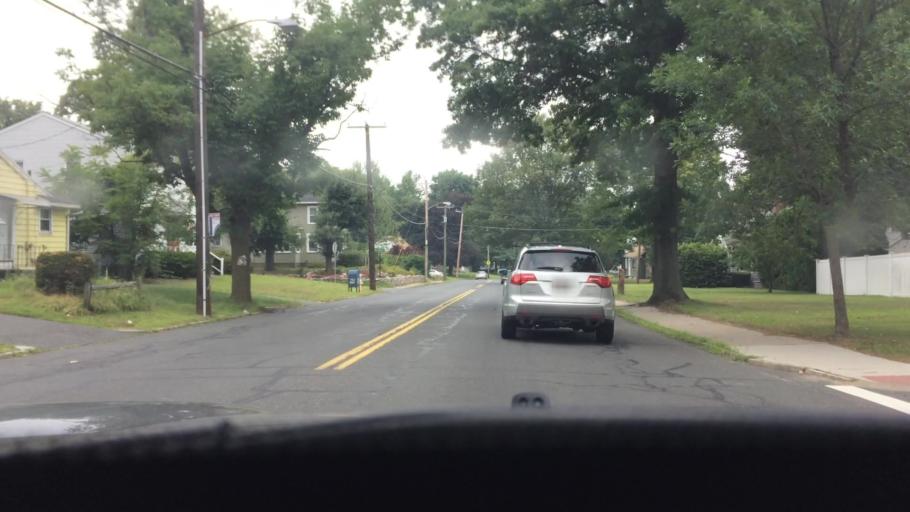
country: US
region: Massachusetts
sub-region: Hampden County
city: Chicopee
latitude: 42.1330
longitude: -72.5847
